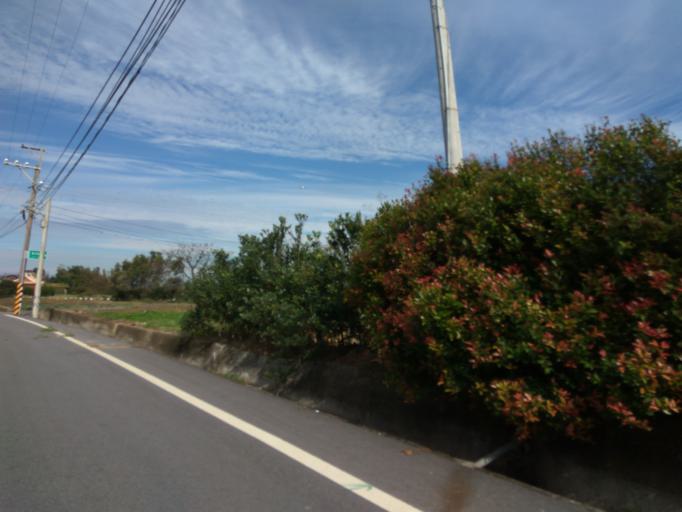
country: TW
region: Taiwan
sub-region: Hsinchu
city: Zhubei
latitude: 25.0019
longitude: 121.0865
